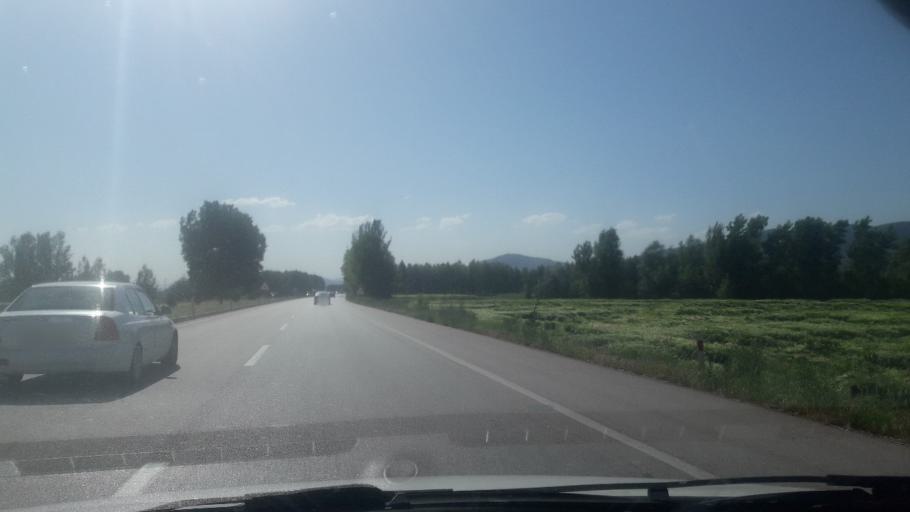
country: TR
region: Tokat
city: Yesilyurt
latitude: 40.3031
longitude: 36.3268
